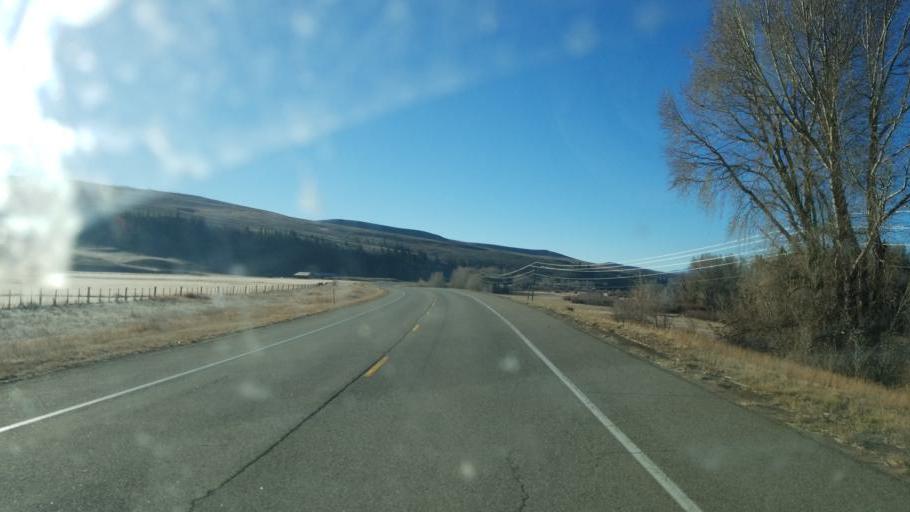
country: US
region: Colorado
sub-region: Gunnison County
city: Gunnison
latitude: 38.7266
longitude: -106.8501
